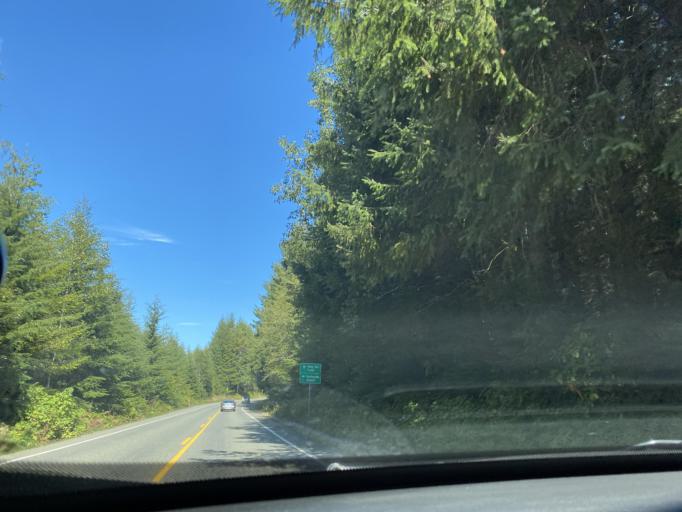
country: US
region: Washington
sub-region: Clallam County
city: Forks
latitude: 47.9497
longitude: -124.4621
